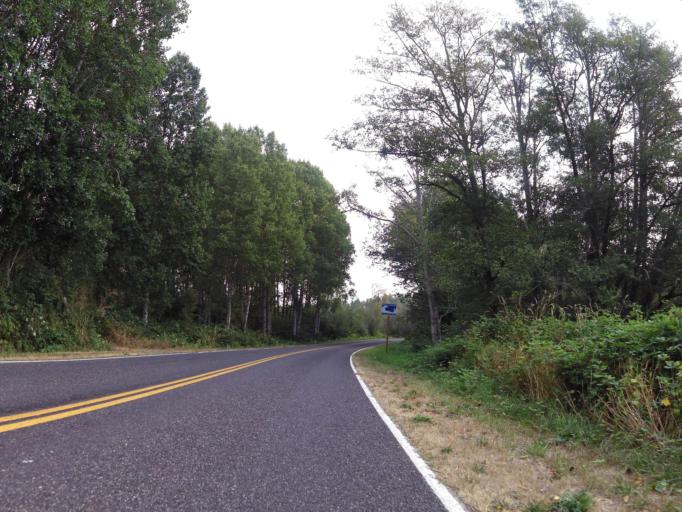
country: US
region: Washington
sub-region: Whatcom County
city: Ferndale
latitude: 48.8070
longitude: -122.6650
